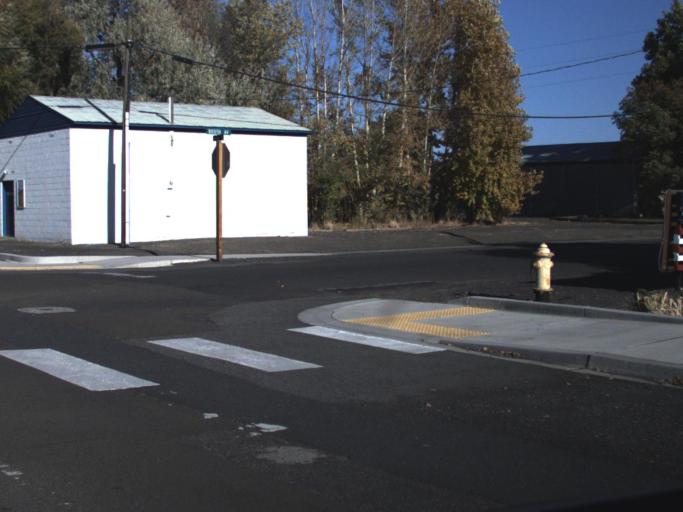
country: US
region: Washington
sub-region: Adams County
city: Ritzville
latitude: 46.7528
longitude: -118.3138
